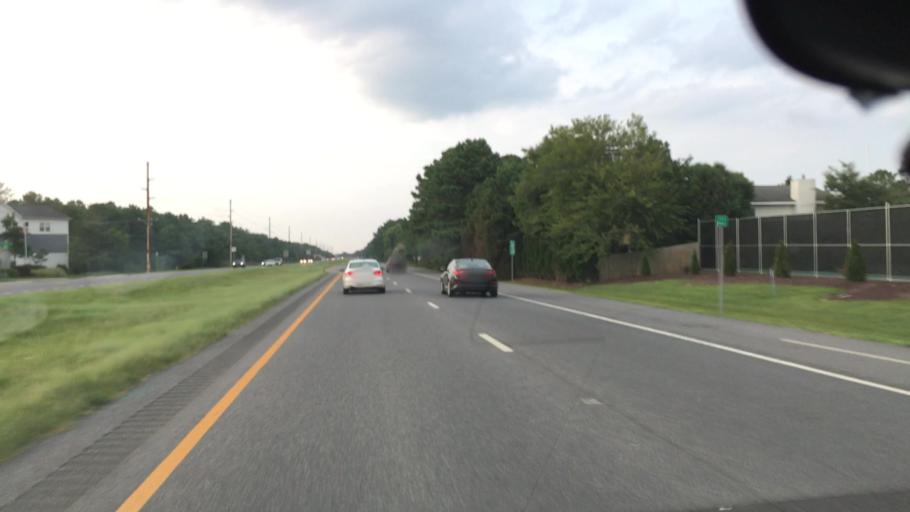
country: US
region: Delaware
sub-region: Sussex County
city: Bethany Beach
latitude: 38.5650
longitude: -75.0602
